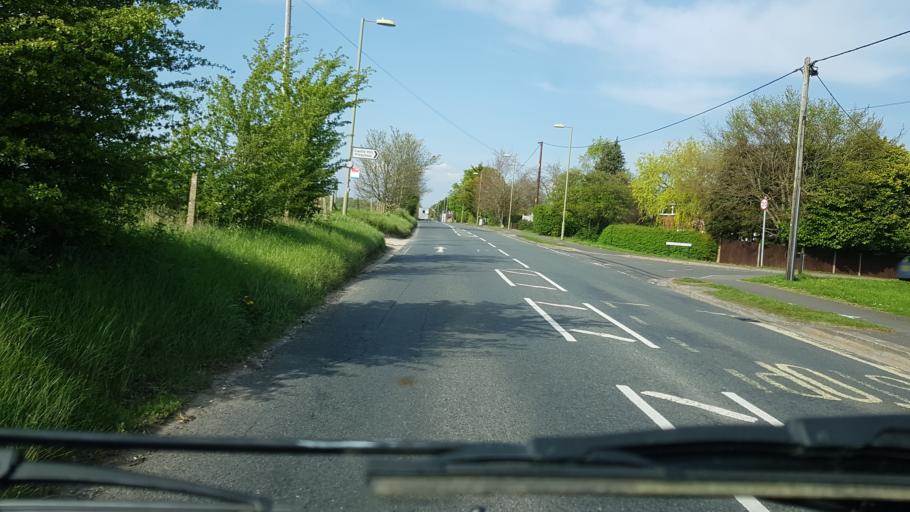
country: GB
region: England
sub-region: Hampshire
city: Basingstoke
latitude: 51.2691
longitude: -1.1308
